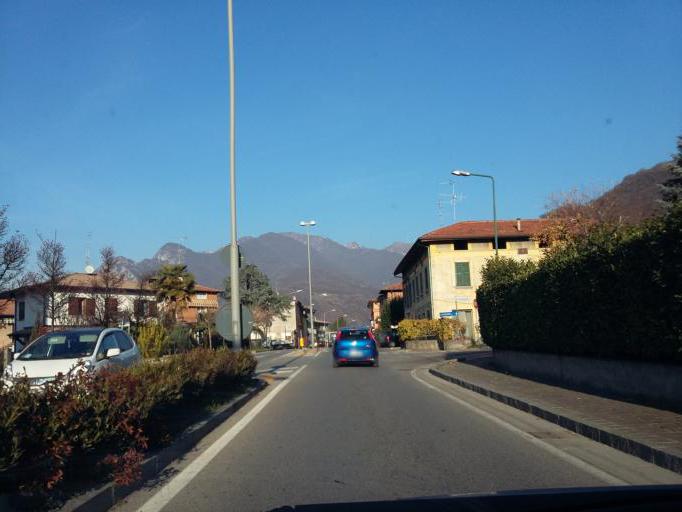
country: IT
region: Lombardy
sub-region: Provincia di Brescia
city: Roe
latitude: 45.6258
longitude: 10.4991
